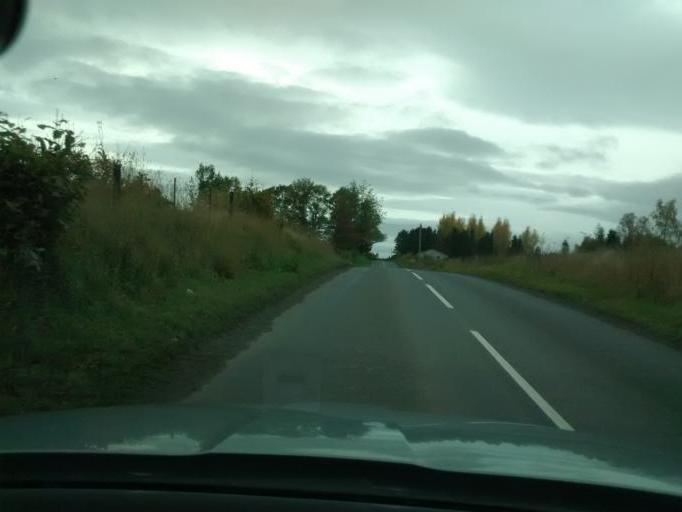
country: GB
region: Scotland
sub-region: Perth and Kinross
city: Stanley
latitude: 56.4960
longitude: -3.4372
